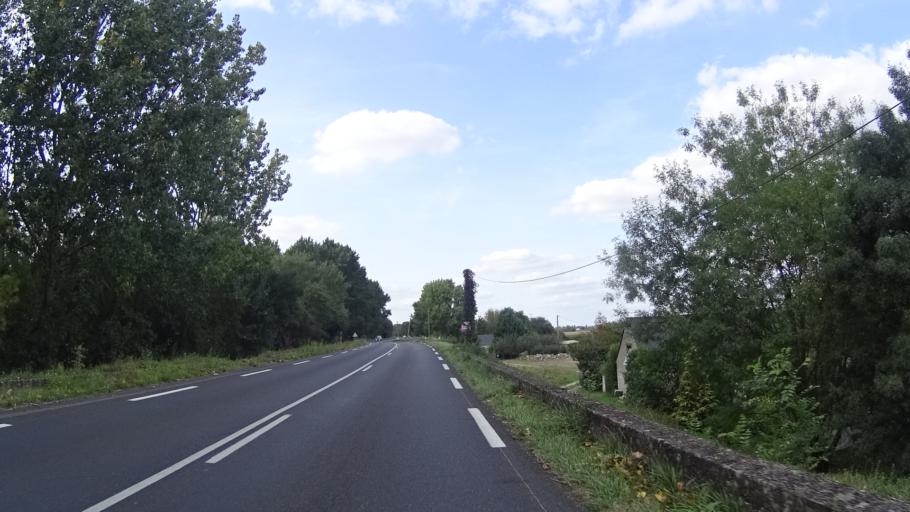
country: FR
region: Pays de la Loire
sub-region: Departement de Maine-et-Loire
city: Gennes
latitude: 47.3672
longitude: -0.2527
